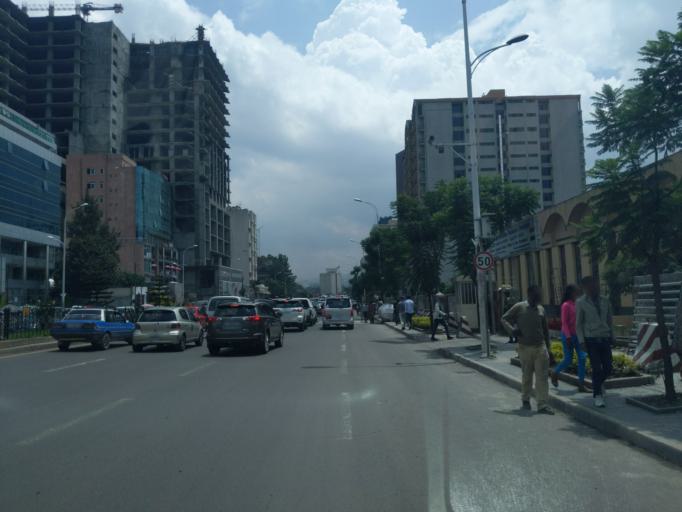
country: ET
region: Adis Abeba
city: Addis Ababa
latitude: 9.0074
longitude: 38.7662
